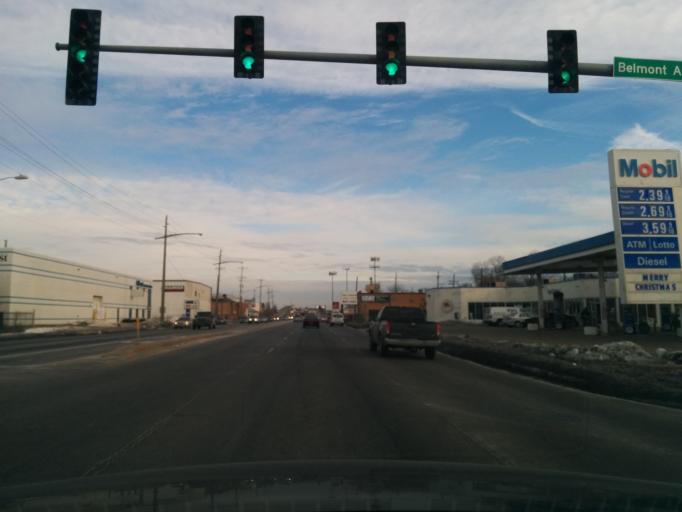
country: US
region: Illinois
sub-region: Cook County
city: Franklin Park
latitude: 41.9364
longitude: -87.8849
